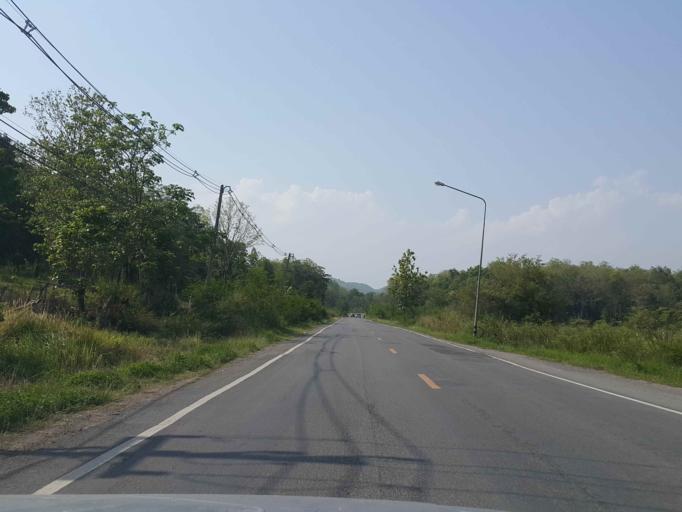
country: TH
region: Chiang Mai
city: Mae On
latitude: 18.8047
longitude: 99.2501
